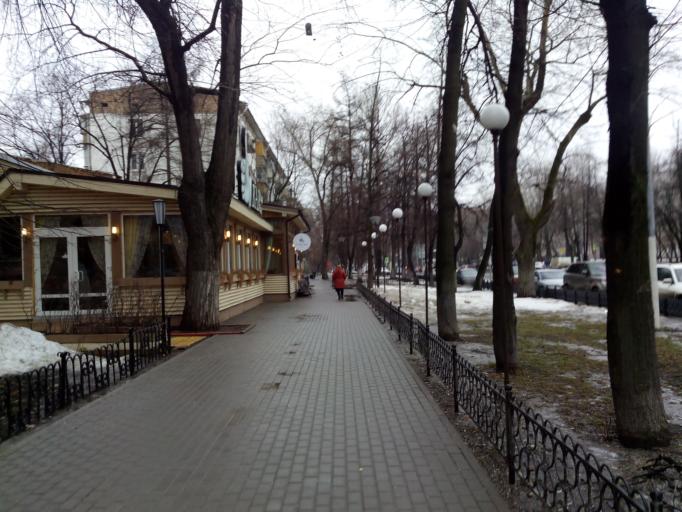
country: RU
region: Moscow
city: Zamoskvorech'ye
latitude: 55.7165
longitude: 37.6085
